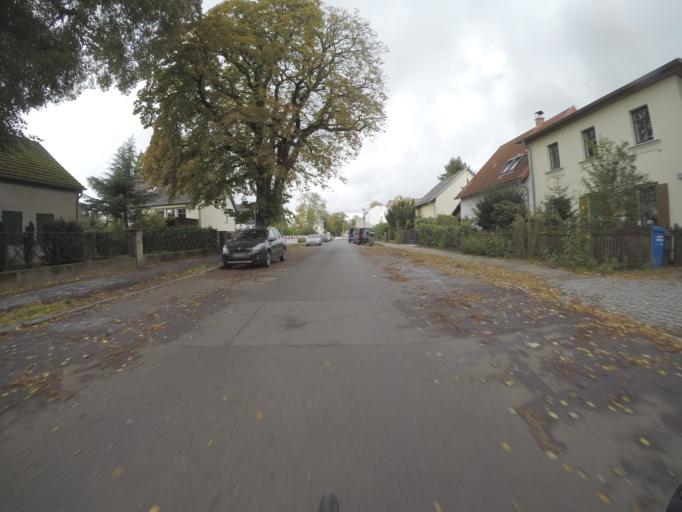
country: DE
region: Berlin
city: Buchholz
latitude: 52.6012
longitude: 13.4300
